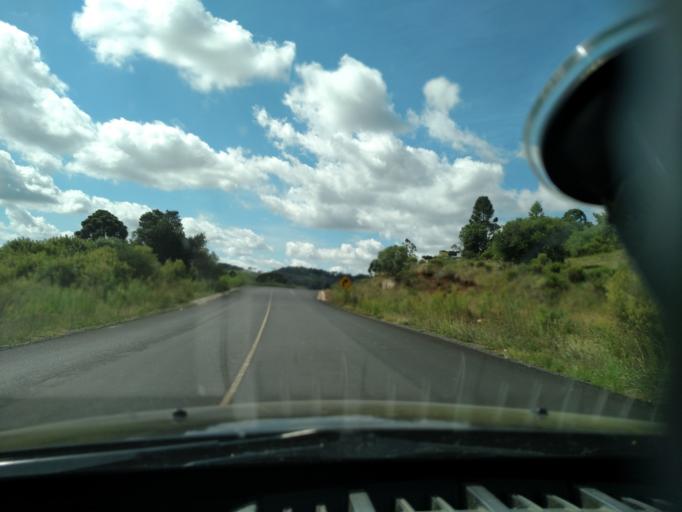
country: BR
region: Santa Catarina
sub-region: Sao Joaquim
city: Sao Joaquim
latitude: -28.0953
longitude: -50.0549
